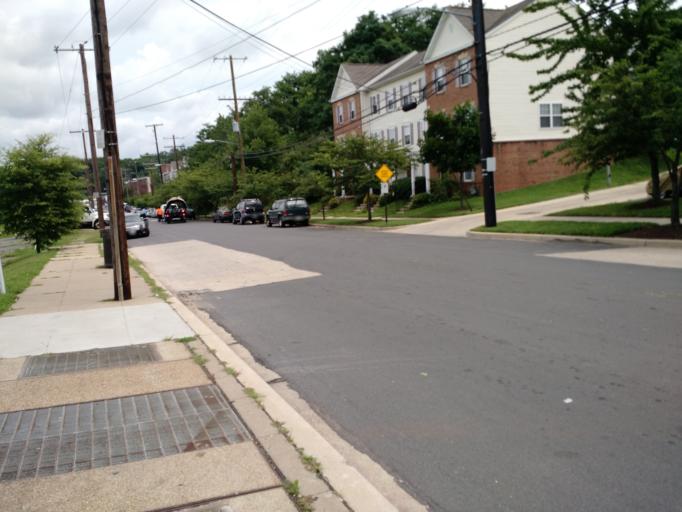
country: US
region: Maryland
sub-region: Prince George's County
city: Glassmanor
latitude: 38.8368
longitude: -76.9929
